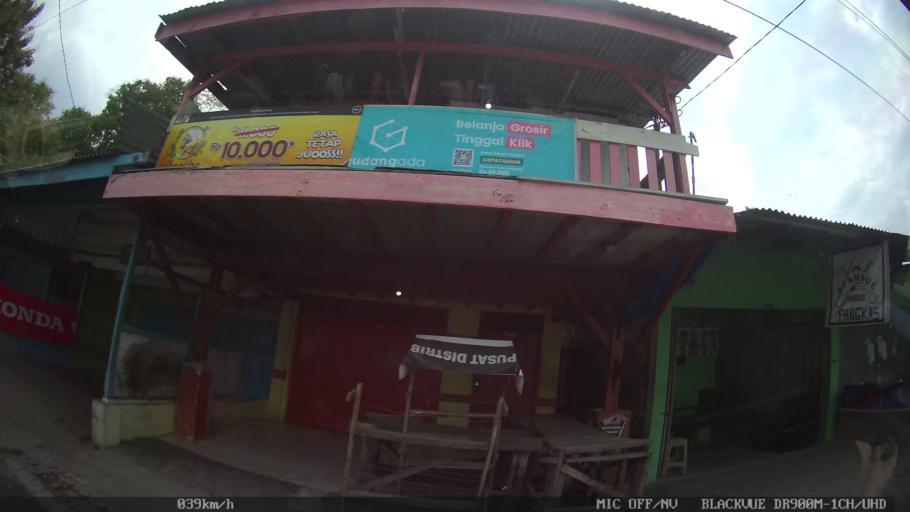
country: ID
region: North Sumatra
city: Sunggal
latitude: 3.6330
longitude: 98.5939
